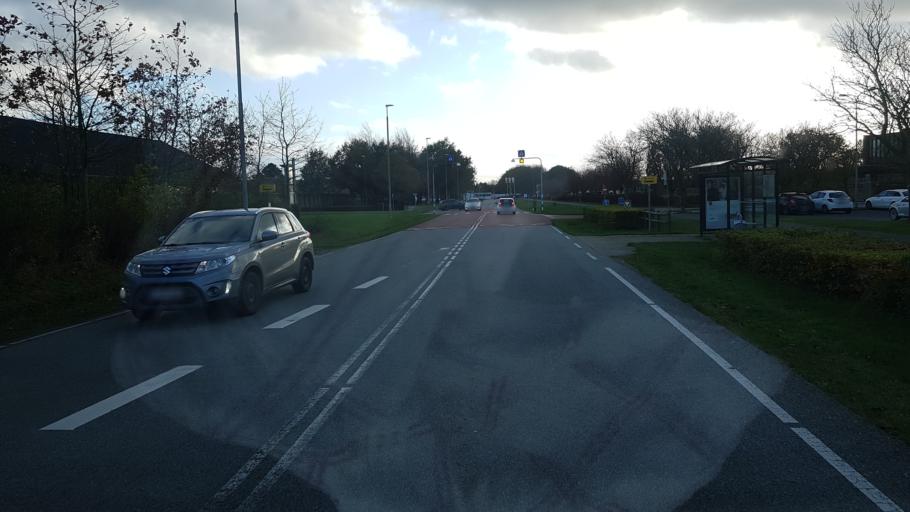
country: DK
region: South Denmark
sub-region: Billund Kommune
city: Grindsted
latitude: 55.7639
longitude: 8.9159
